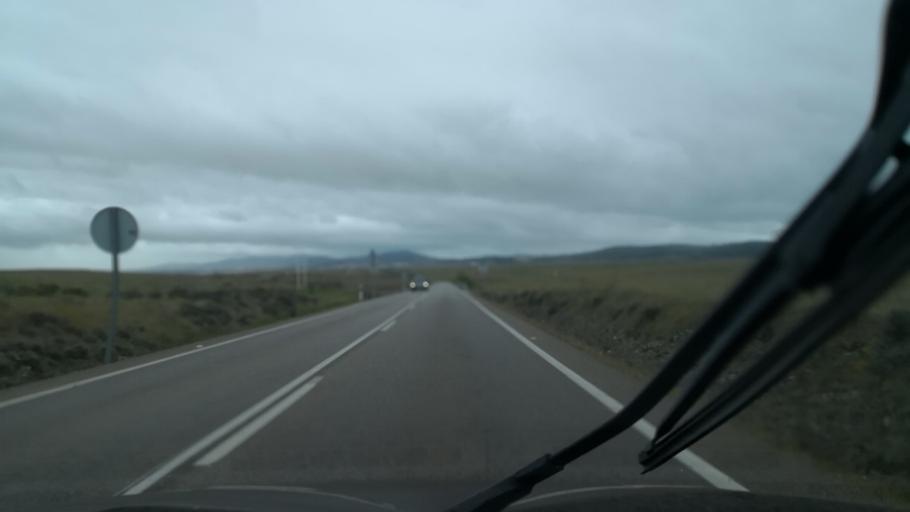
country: ES
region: Extremadura
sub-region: Provincia de Caceres
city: Casar de Caceres
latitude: 39.5340
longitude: -6.4057
